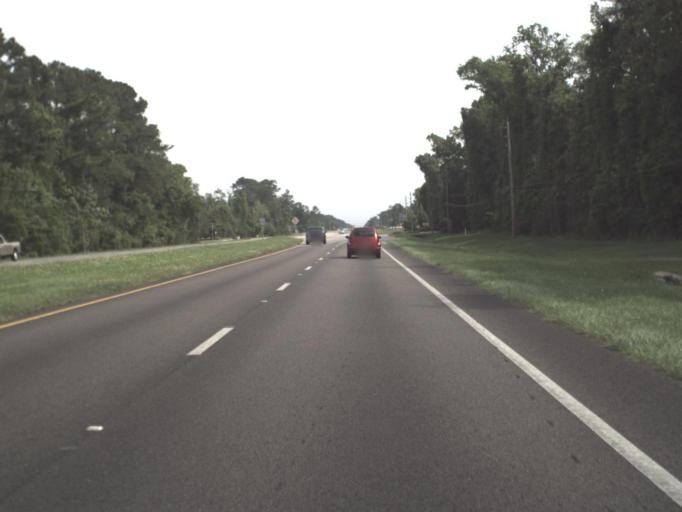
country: US
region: Florida
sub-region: Clay County
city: Green Cove Springs
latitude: 30.0532
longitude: -81.7080
